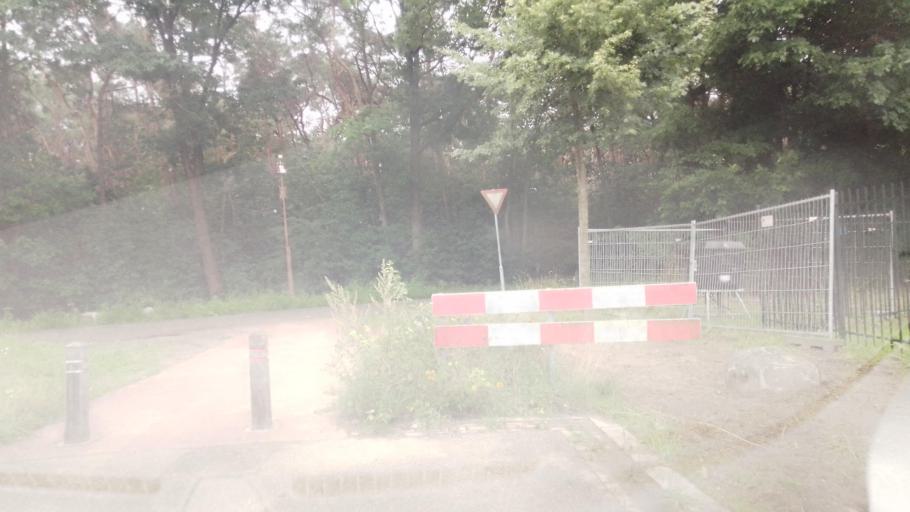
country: NL
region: Limburg
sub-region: Gemeente Peel en Maas
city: Maasbree
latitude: 51.4063
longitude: 6.1005
